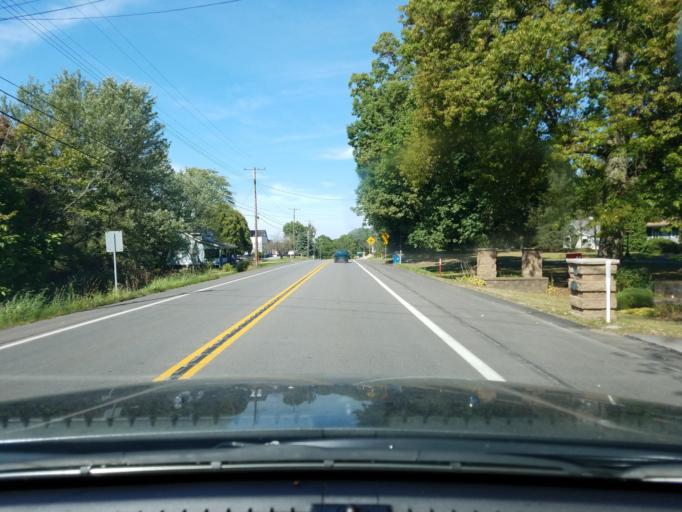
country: US
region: Pennsylvania
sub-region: Lawrence County
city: New Castle
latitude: 40.9512
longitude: -80.2852
